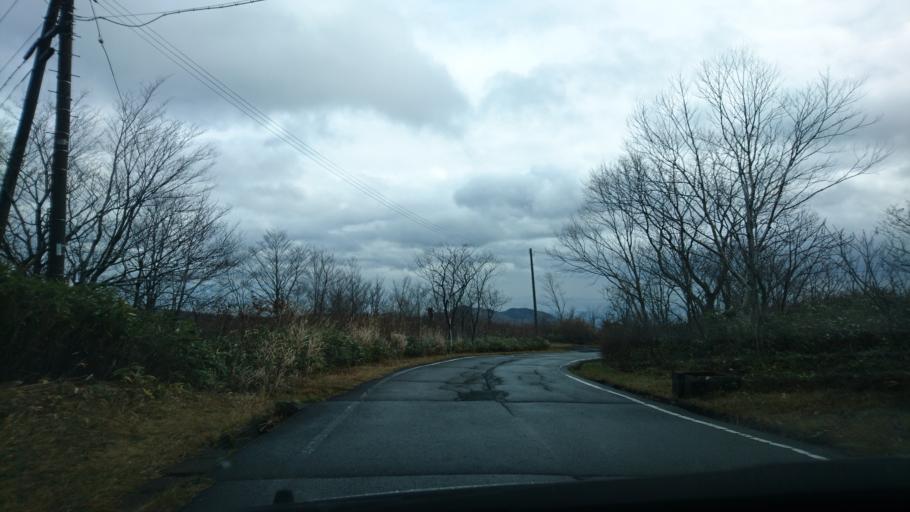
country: JP
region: Iwate
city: Ichinoseki
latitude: 38.9417
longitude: 140.8200
